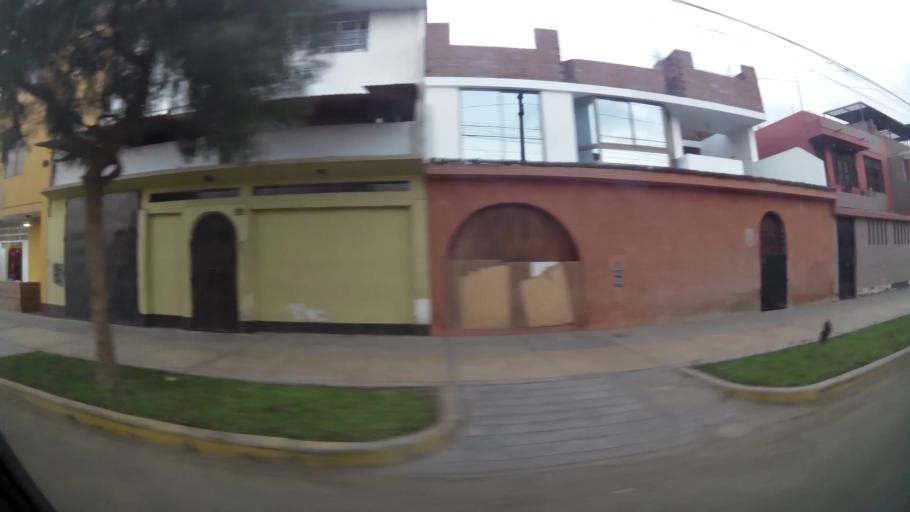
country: PE
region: La Libertad
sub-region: Provincia de Trujillo
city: El Porvenir
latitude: -8.0949
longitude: -79.0191
